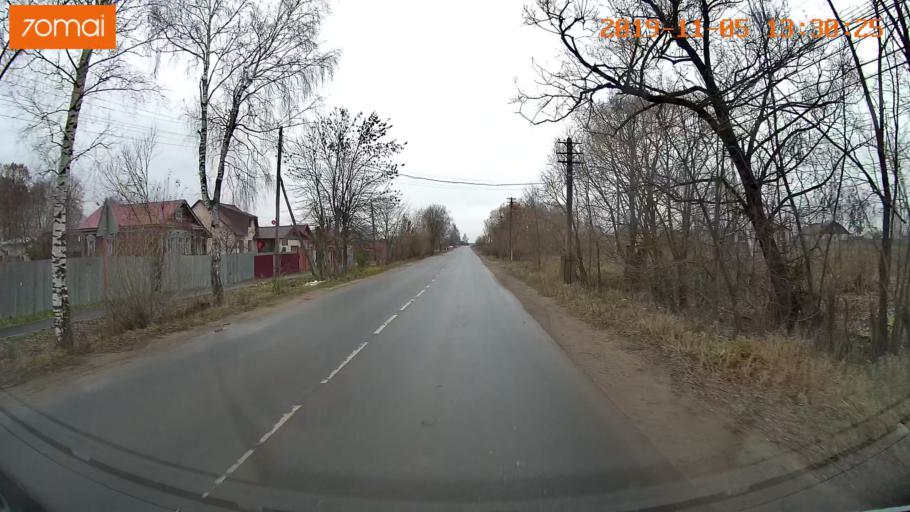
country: RU
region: Ivanovo
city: Shuya
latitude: 56.8669
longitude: 41.3963
